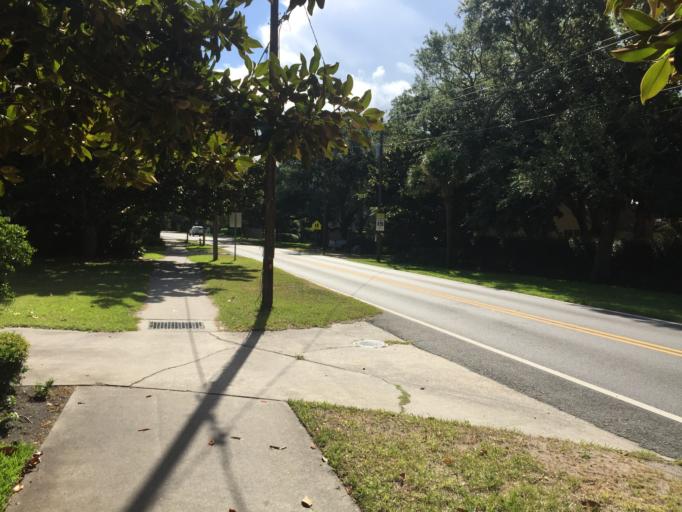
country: US
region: Georgia
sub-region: Glynn County
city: Saint Simons Island
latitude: 31.1355
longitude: -81.3886
